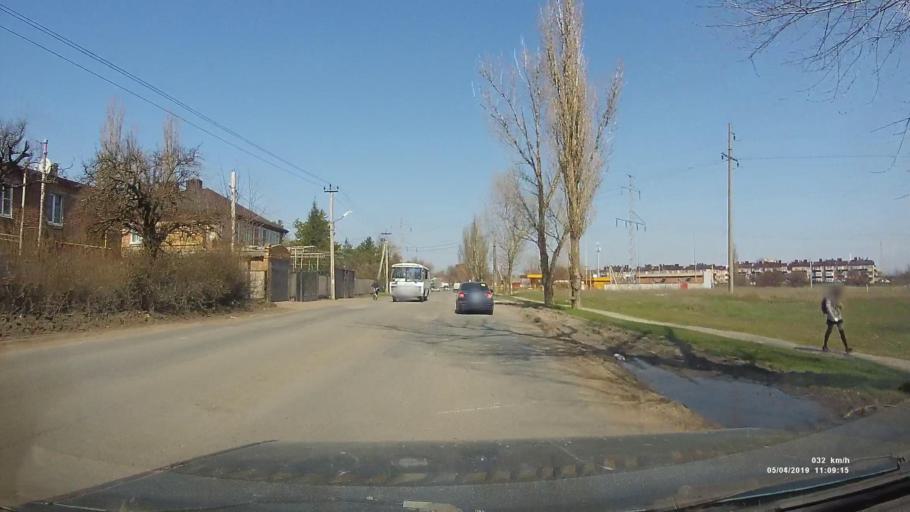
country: RU
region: Rostov
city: Azov
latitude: 47.0897
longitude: 39.4333
